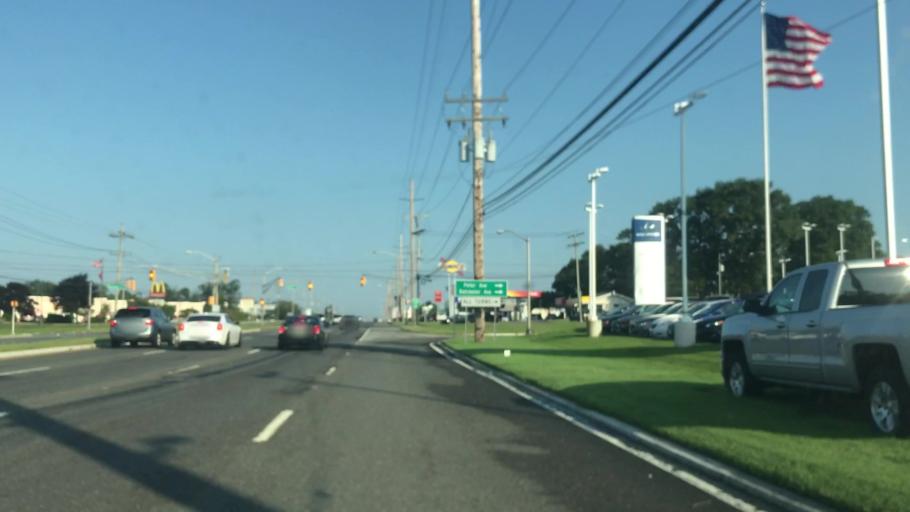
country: US
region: New Jersey
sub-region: Ocean County
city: Pine Beach
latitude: 39.9572
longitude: -74.1691
